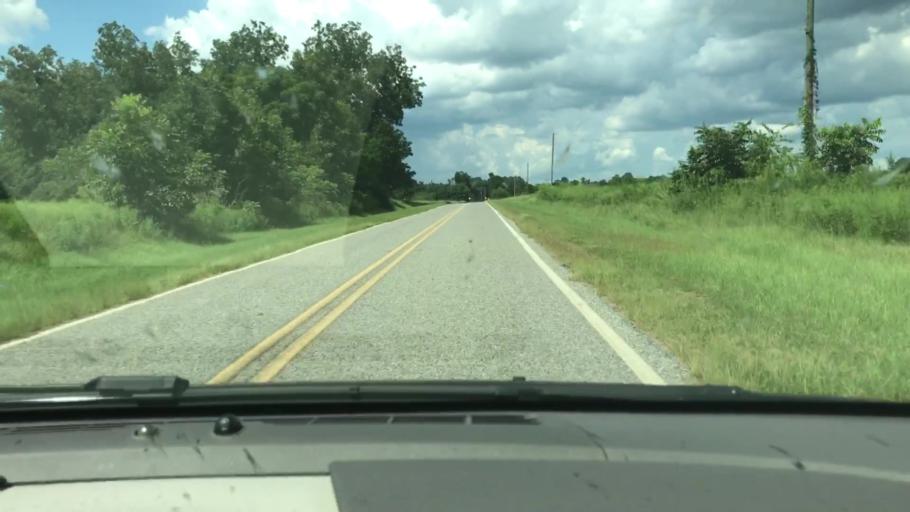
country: US
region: Georgia
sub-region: Quitman County
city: Georgetown
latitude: 31.7536
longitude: -85.0742
